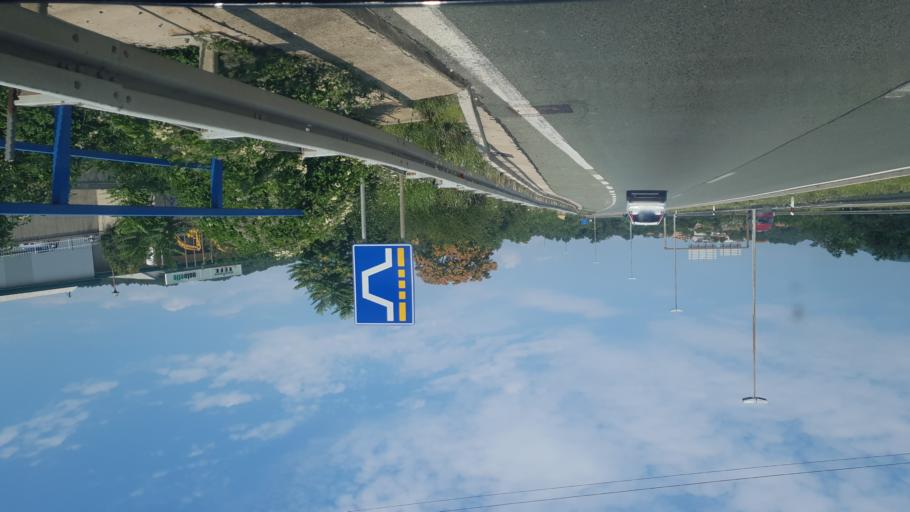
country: HR
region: Primorsko-Goranska
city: Matulji
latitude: 45.3663
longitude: 14.3296
